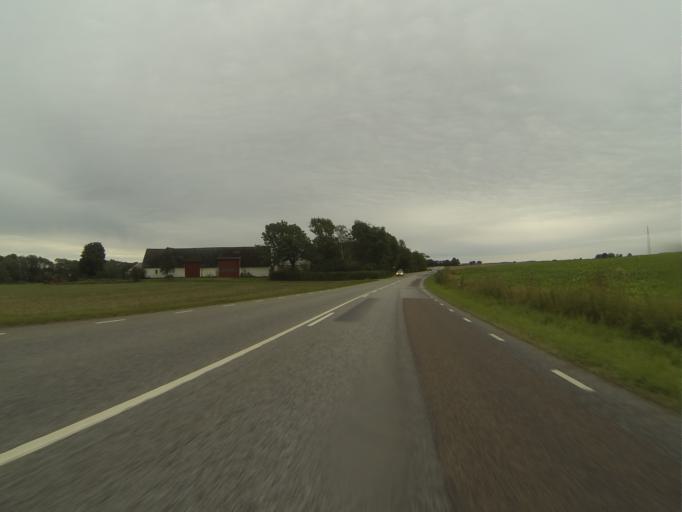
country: SE
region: Skane
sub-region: Svedala Kommun
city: Klagerup
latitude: 55.6273
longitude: 13.3013
